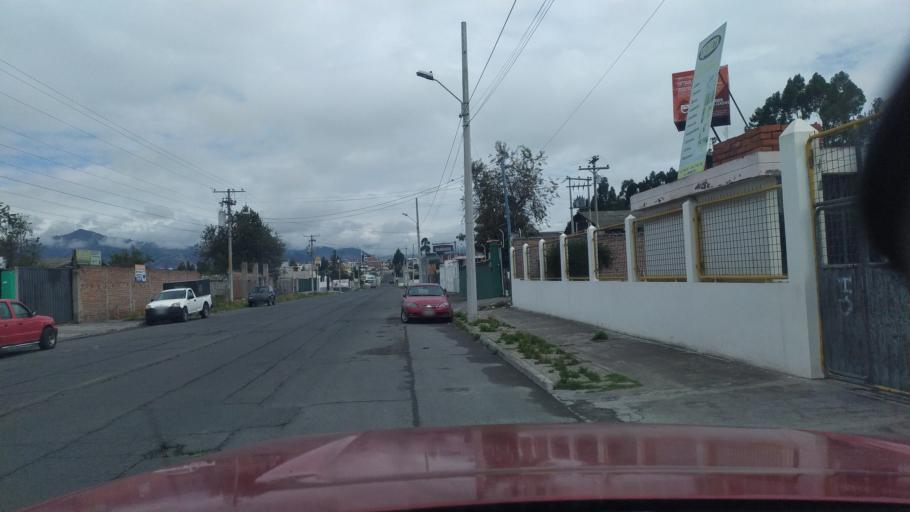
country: EC
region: Chimborazo
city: Riobamba
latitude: -1.6785
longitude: -78.6337
